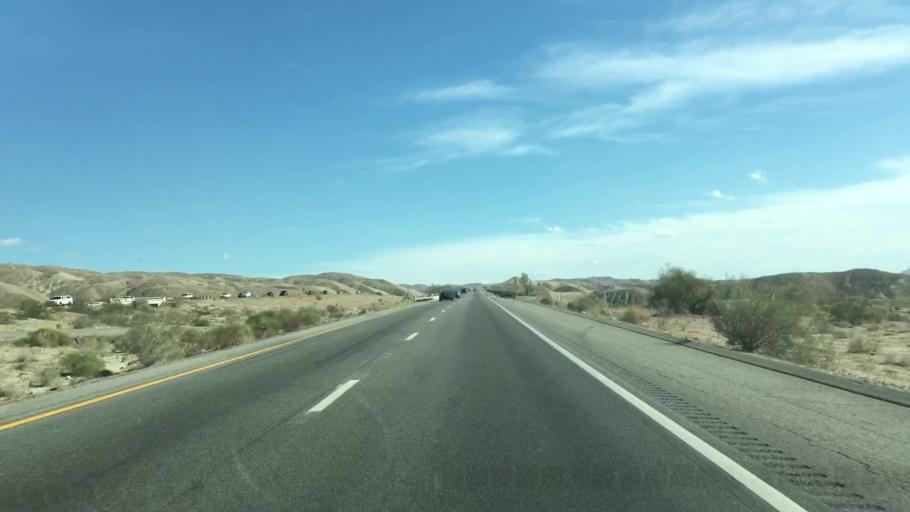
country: US
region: California
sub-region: Riverside County
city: Coachella
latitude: 33.7021
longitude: -116.1251
